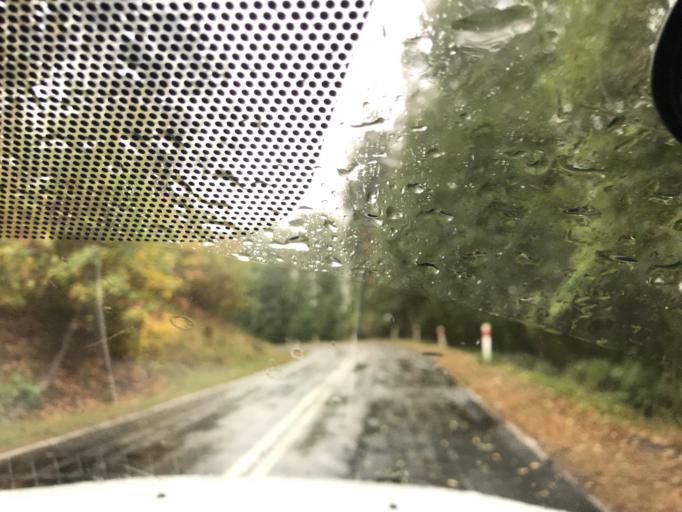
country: DE
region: Brandenburg
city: Neulewin
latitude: 52.7829
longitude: 14.2922
